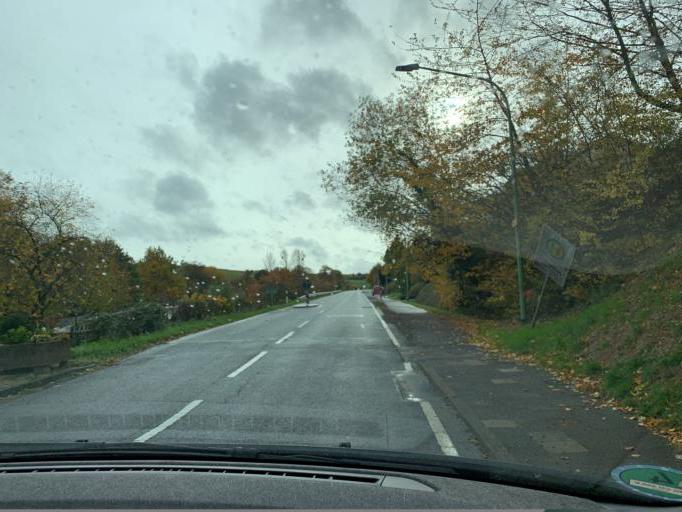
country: DE
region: North Rhine-Westphalia
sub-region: Regierungsbezirk Koln
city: Kreuzau
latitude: 50.7249
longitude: 6.4766
